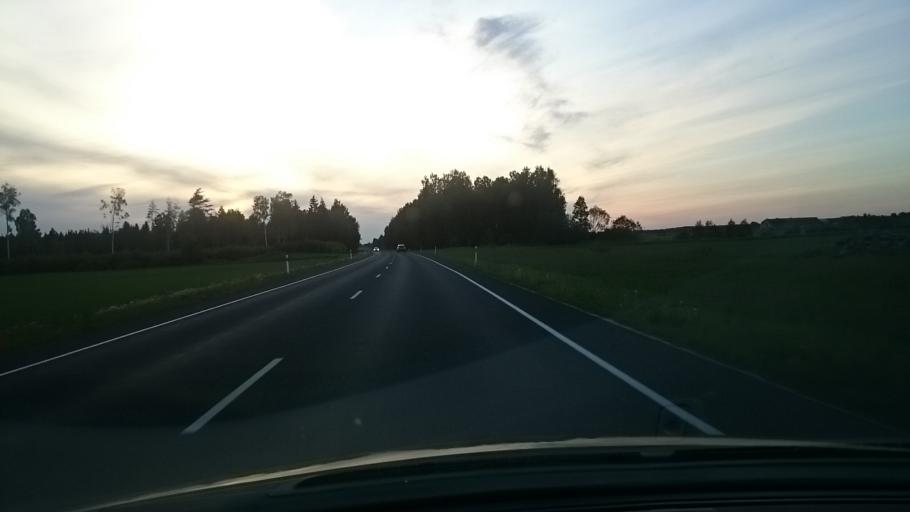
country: EE
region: Viljandimaa
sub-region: Vohma linn
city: Vohma
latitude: 58.7375
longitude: 25.5866
